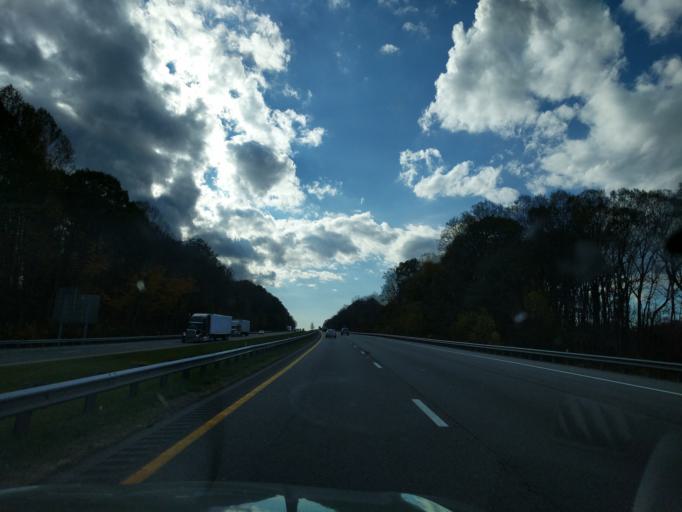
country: US
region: Virginia
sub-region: Wythe County
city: Rural Retreat
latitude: 36.9153
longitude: -81.2777
